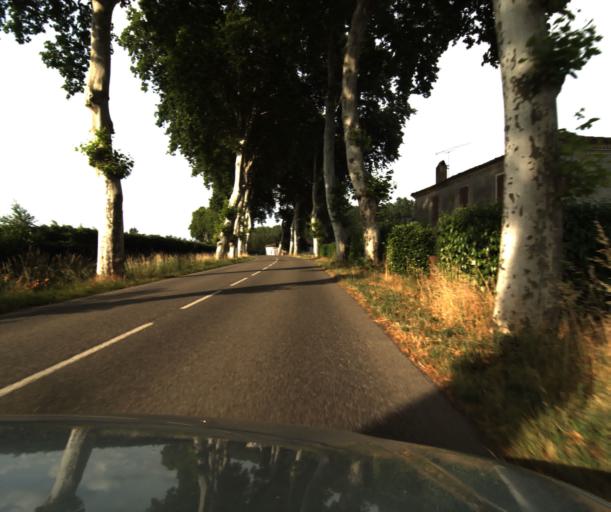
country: FR
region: Midi-Pyrenees
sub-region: Departement du Tarn-et-Garonne
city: Beaumont-de-Lomagne
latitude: 43.8488
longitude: 0.9393
